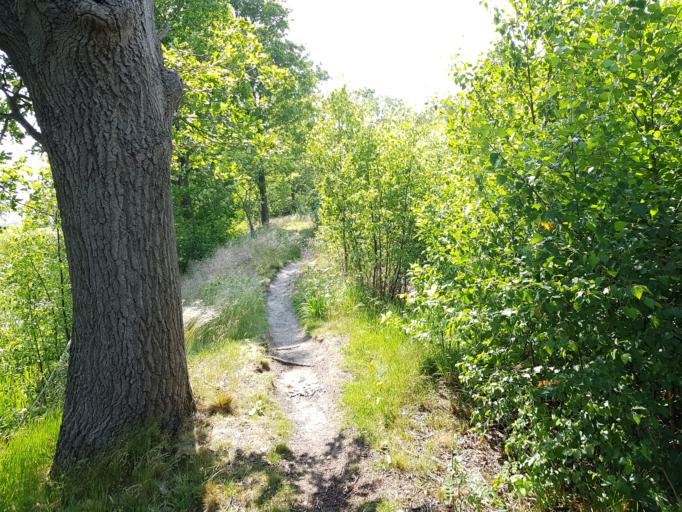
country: NL
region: Friesland
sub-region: Gemeente Heerenveen
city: Jubbega
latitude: 53.0503
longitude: 6.1139
